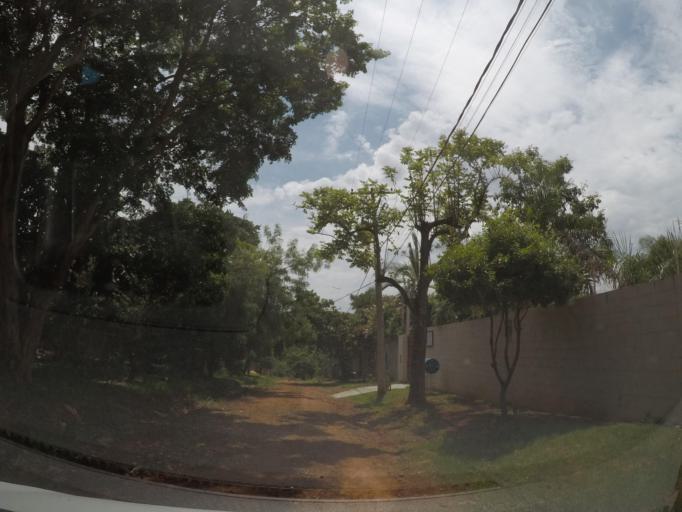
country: BR
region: Sao Paulo
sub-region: Sumare
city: Sumare
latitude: -22.8482
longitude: -47.2991
